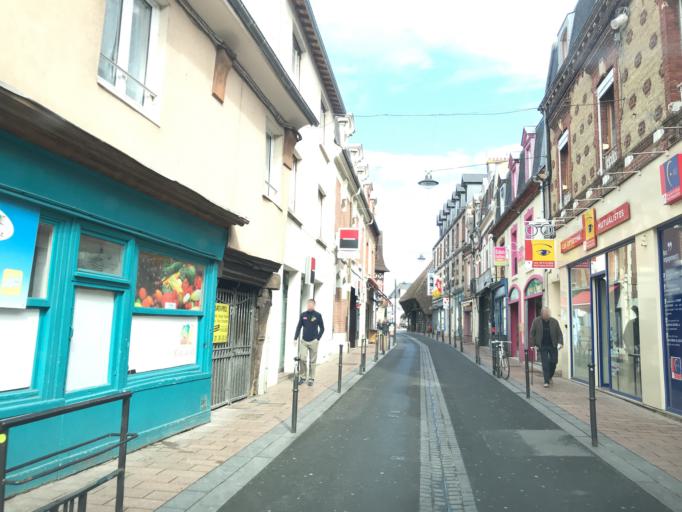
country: FR
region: Lower Normandy
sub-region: Departement du Calvados
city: Dives-sur-Mer
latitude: 49.2857
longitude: -0.0973
